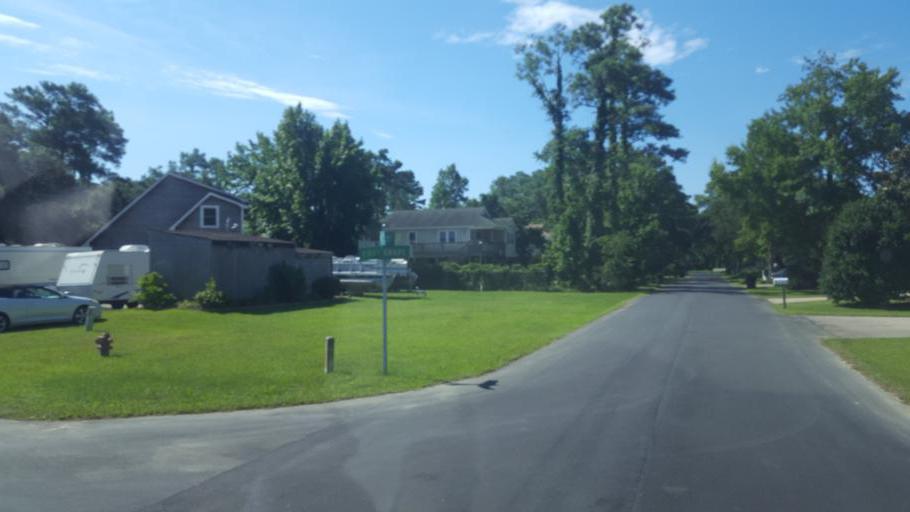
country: US
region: North Carolina
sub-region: Dare County
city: Kill Devil Hills
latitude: 36.0086
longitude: -75.6777
